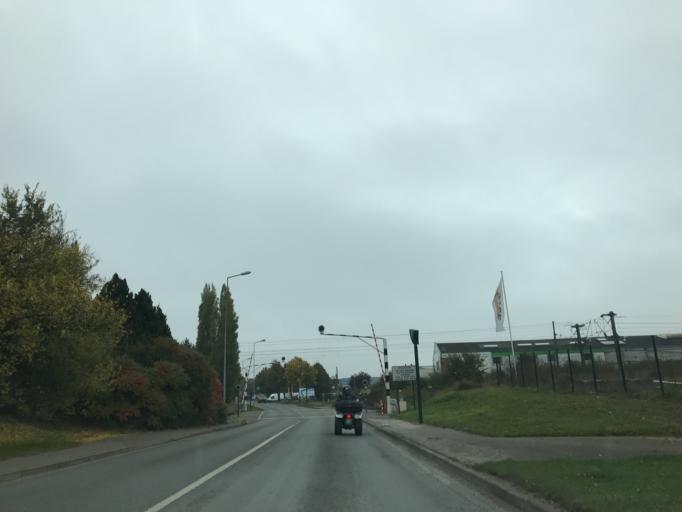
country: FR
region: Nord-Pas-de-Calais
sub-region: Departement du Pas-de-Calais
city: Saint-Laurent-Blangy
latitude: 50.2935
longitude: 2.8052
